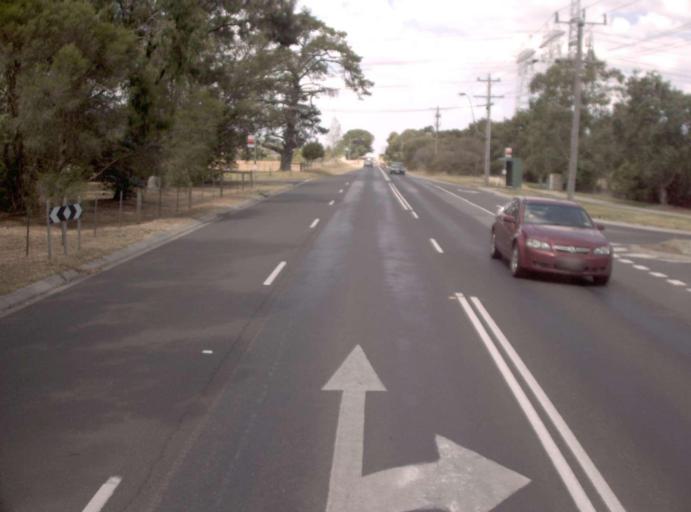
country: AU
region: Victoria
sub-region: Casey
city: Narre Warren South
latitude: -38.0304
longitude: 145.2838
